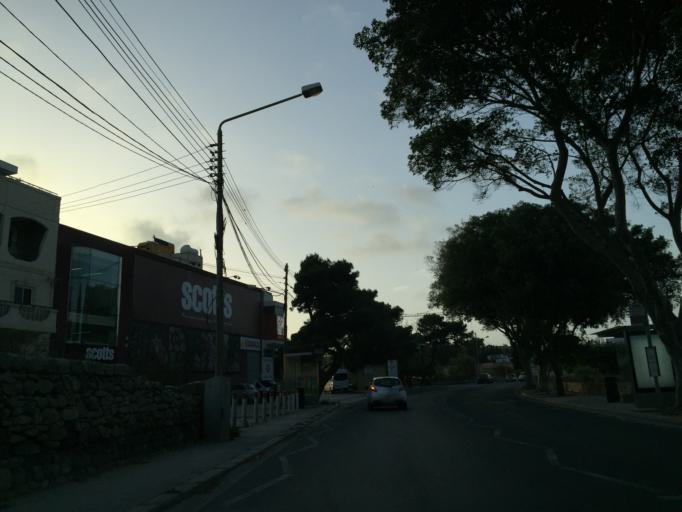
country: MT
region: Saint Paul's Bay
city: San Pawl il-Bahar
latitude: 35.9374
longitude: 14.4119
